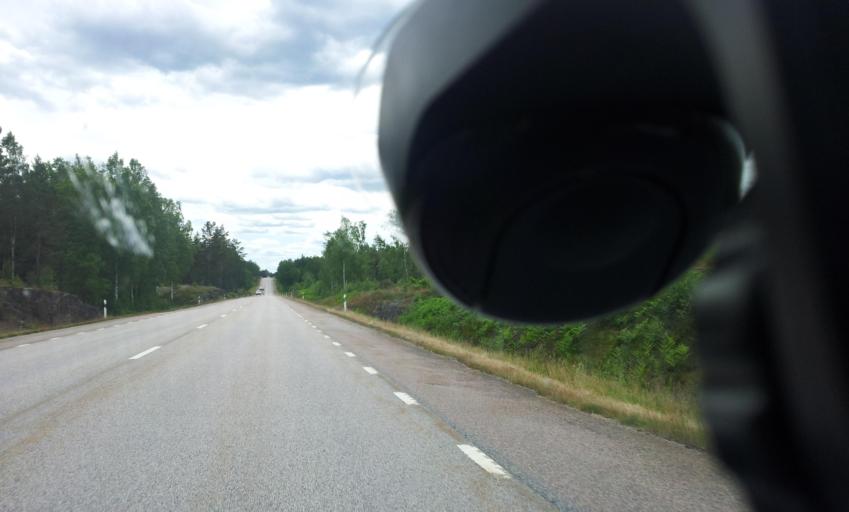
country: SE
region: Kalmar
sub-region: Oskarshamns Kommun
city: Oskarshamn
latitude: 57.4713
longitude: 16.5173
